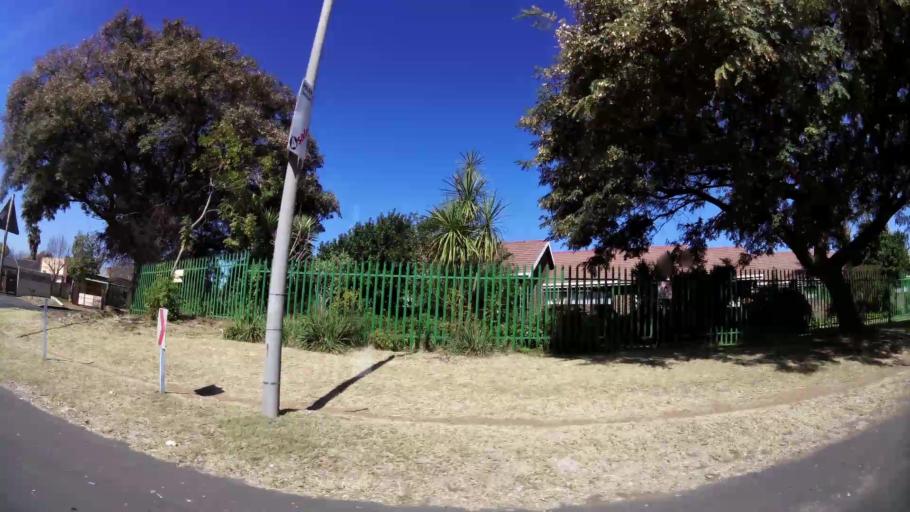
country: ZA
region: Gauteng
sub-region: Ekurhuleni Metropolitan Municipality
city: Tembisa
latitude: -26.0484
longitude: 28.2346
